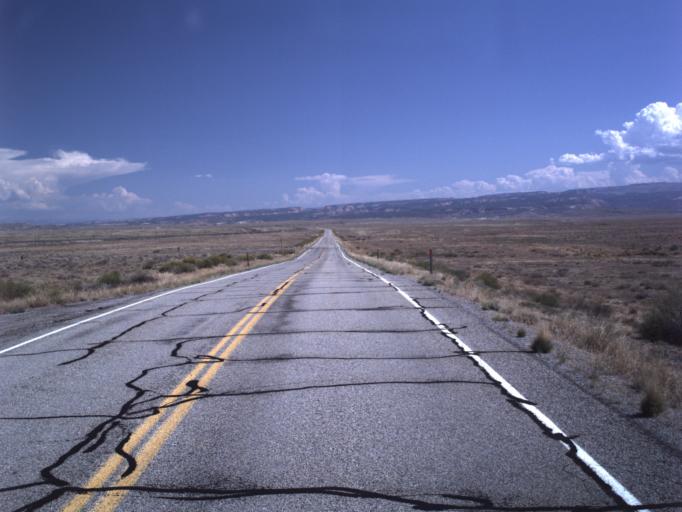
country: US
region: Utah
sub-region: Grand County
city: Moab
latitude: 38.9408
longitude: -109.3806
